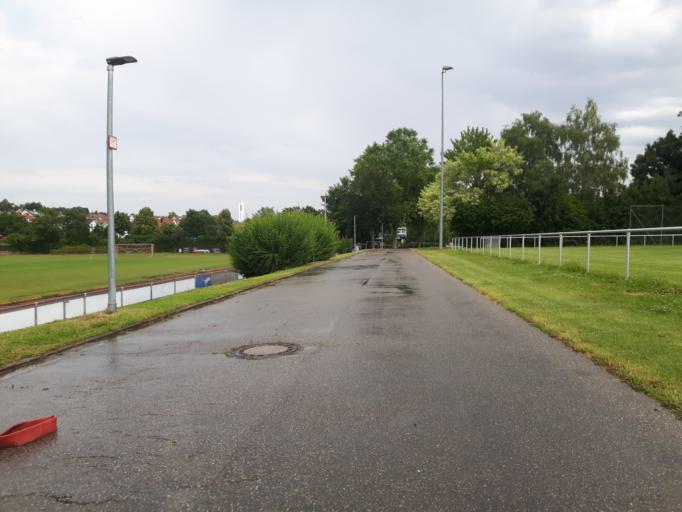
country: DE
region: Baden-Wuerttemberg
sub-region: Regierungsbezirk Stuttgart
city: Schwaigern
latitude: 49.1449
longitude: 9.0461
